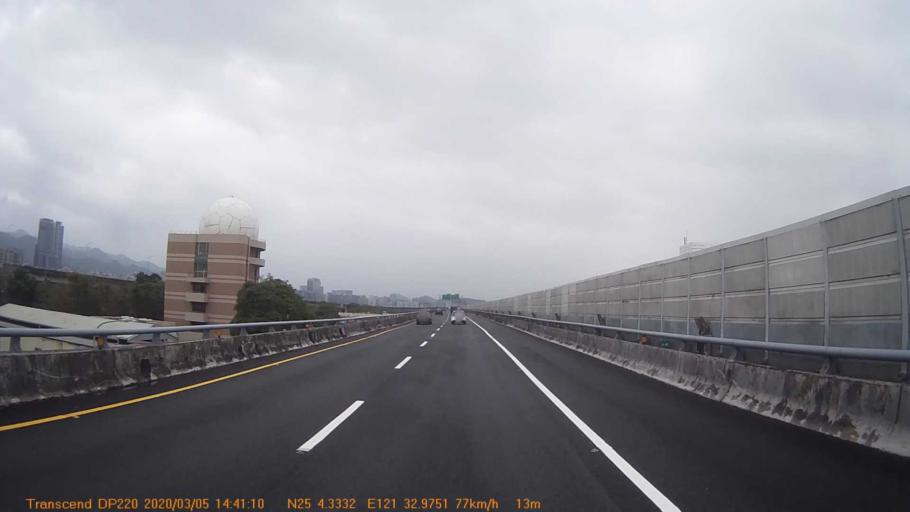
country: TW
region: Taipei
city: Taipei
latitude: 25.0722
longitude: 121.5499
